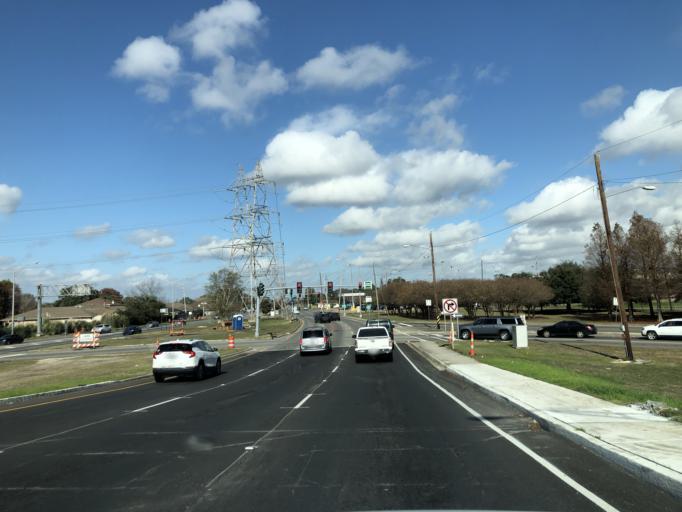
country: US
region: Louisiana
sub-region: Jefferson Parish
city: Kenner
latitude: 30.0095
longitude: -90.2214
